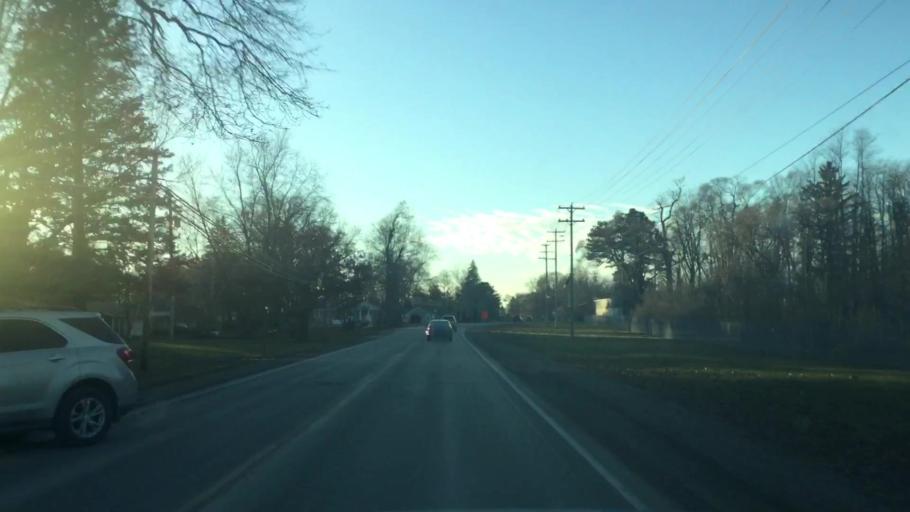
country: US
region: Michigan
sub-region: Genesee County
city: Linden
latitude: 42.8108
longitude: -83.8041
